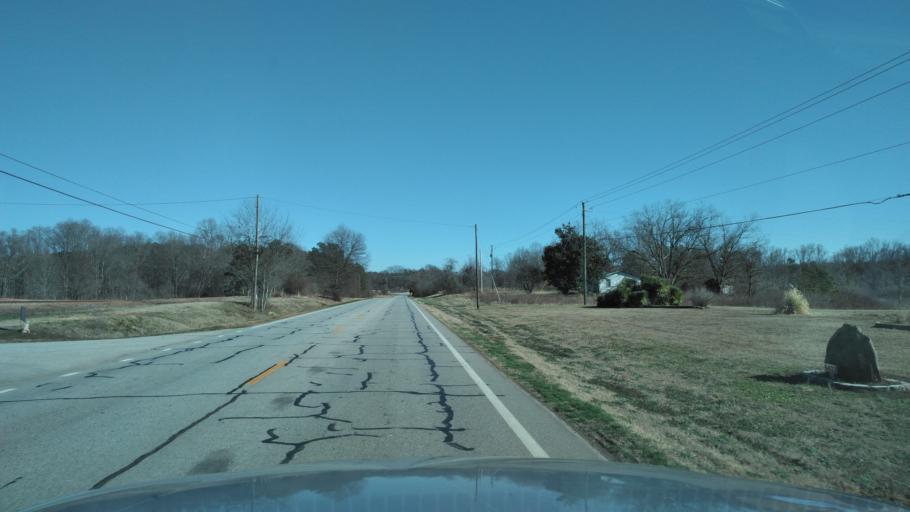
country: US
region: Georgia
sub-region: Banks County
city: Maysville
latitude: 34.2401
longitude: -83.5208
